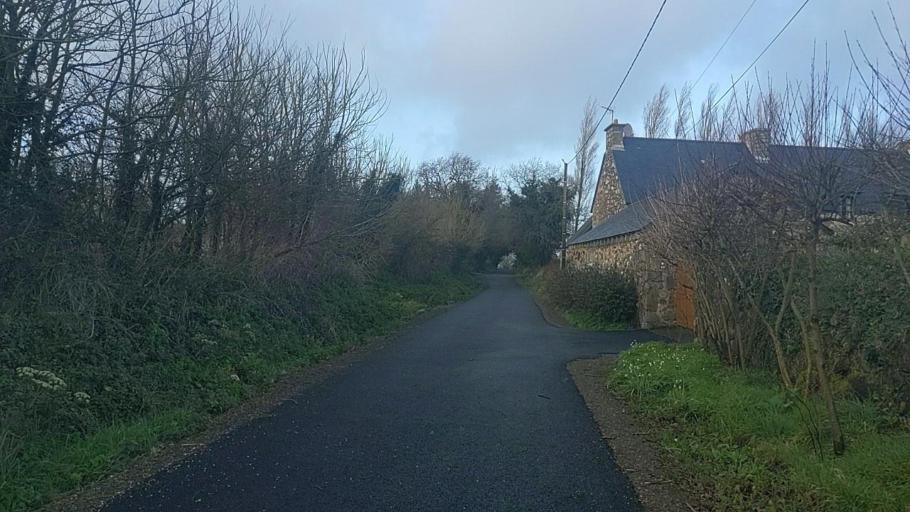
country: FR
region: Brittany
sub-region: Departement des Cotes-d'Armor
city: Plougrescant
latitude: 48.8289
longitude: -3.1900
